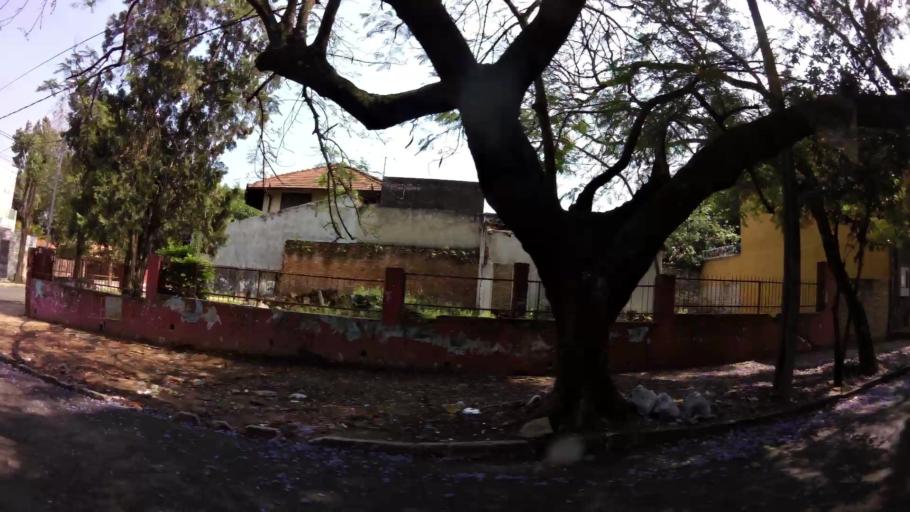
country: PY
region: Presidente Hayes
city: Nanawa
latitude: -25.2882
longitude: -57.6581
